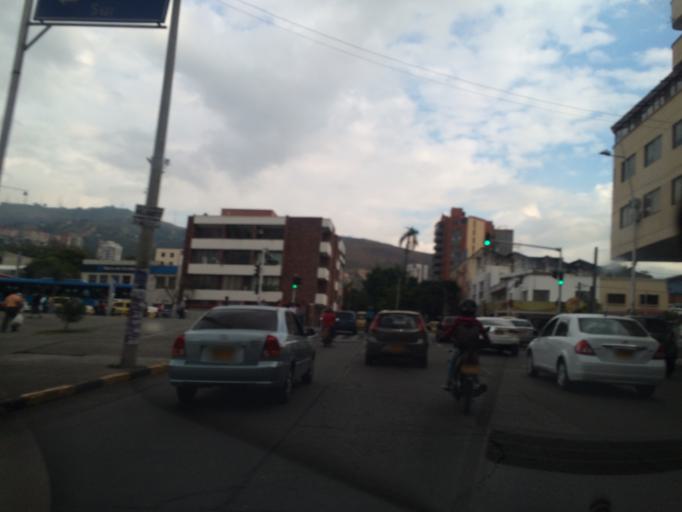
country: CO
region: Valle del Cauca
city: Cali
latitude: 3.4324
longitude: -76.5422
